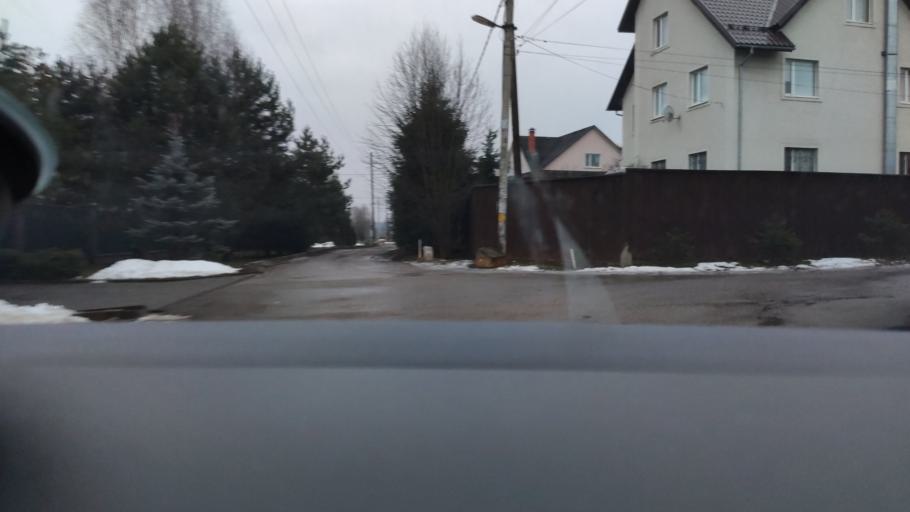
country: RU
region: Moskovskaya
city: Zvenigorod
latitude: 55.7442
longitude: 36.9427
